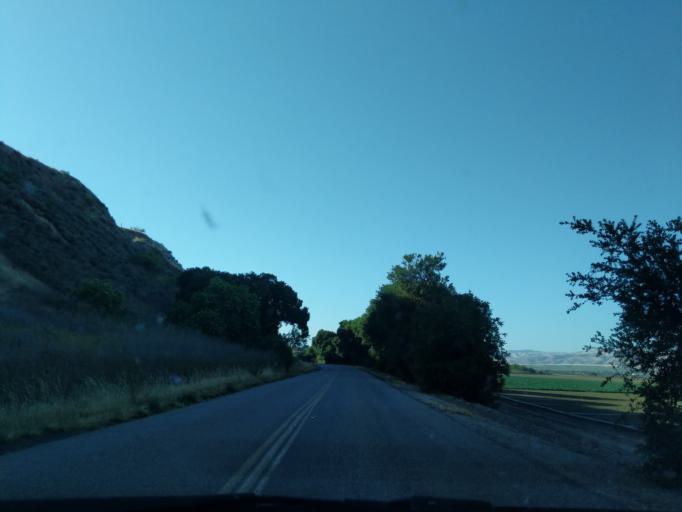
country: US
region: California
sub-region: Monterey County
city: Soledad
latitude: 36.4195
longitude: -121.3993
